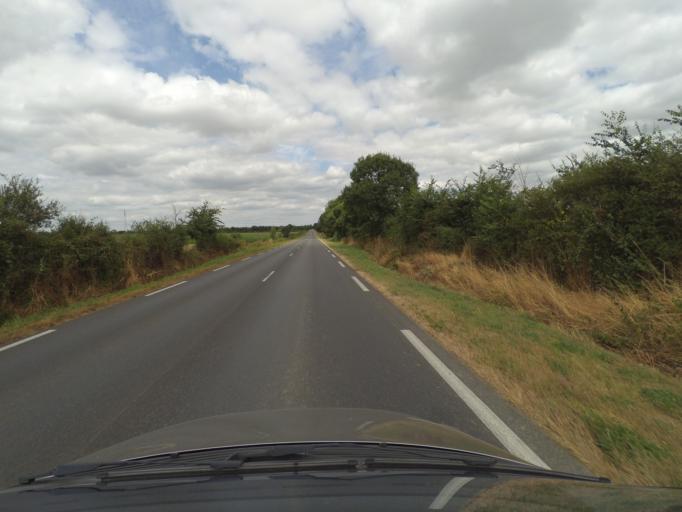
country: FR
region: Pays de la Loire
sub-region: Departement de Maine-et-Loire
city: Le Longeron
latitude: 47.0458
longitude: -1.0695
